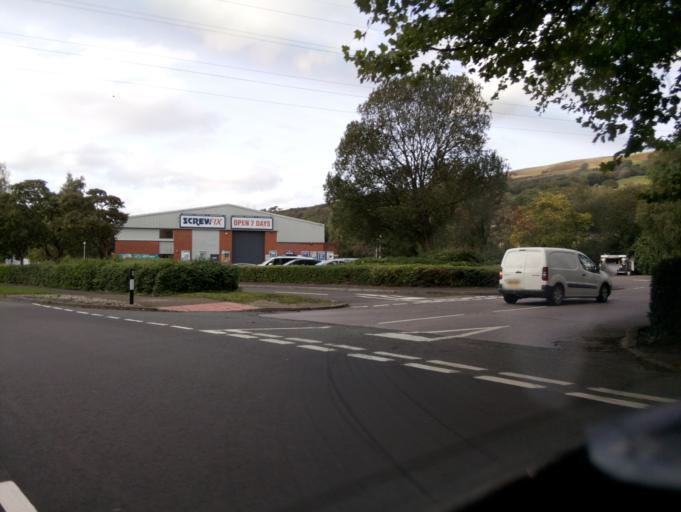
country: GB
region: Wales
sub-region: Caerphilly County Borough
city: Abertridwr
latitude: 51.5739
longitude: -3.2902
